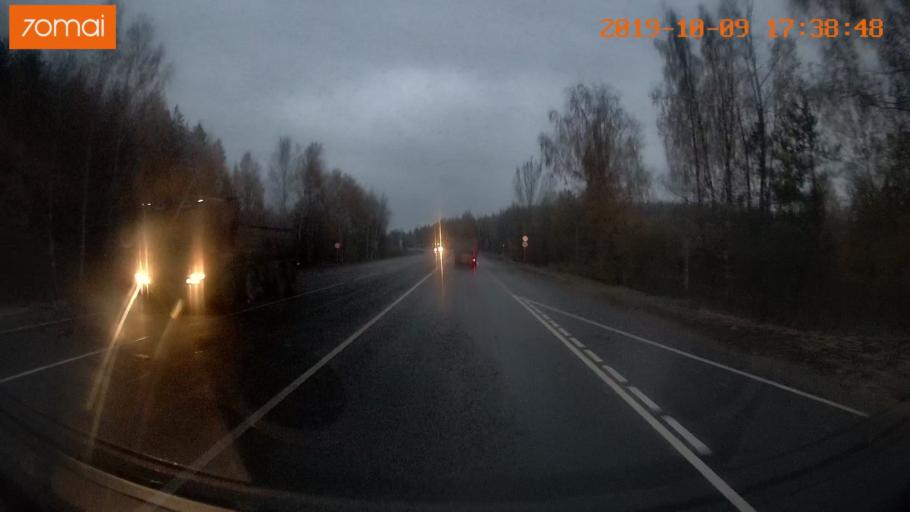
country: RU
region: Ivanovo
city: Bogorodskoye
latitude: 57.0671
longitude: 40.9522
